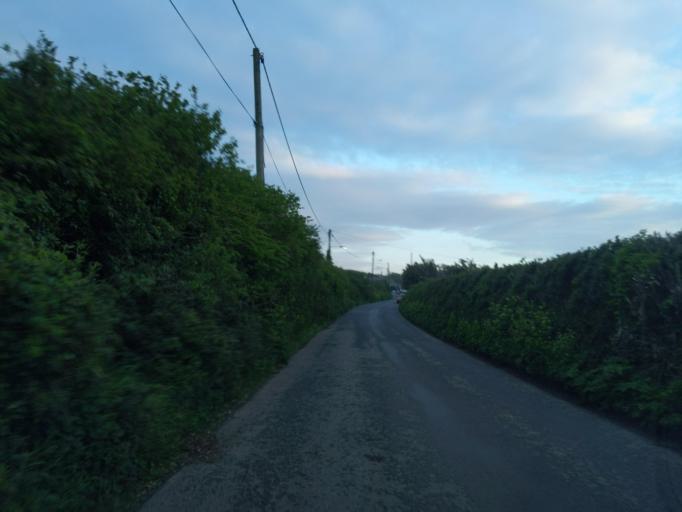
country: GB
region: England
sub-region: Cornwall
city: Polzeath
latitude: 50.5615
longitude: -4.8723
